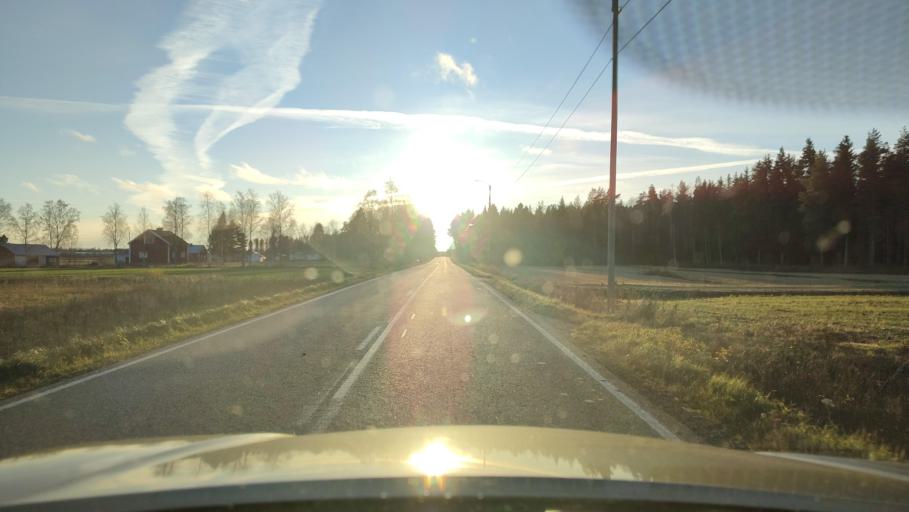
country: FI
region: Ostrobothnia
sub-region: Vaasa
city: Malax
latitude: 62.7001
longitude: 21.5815
